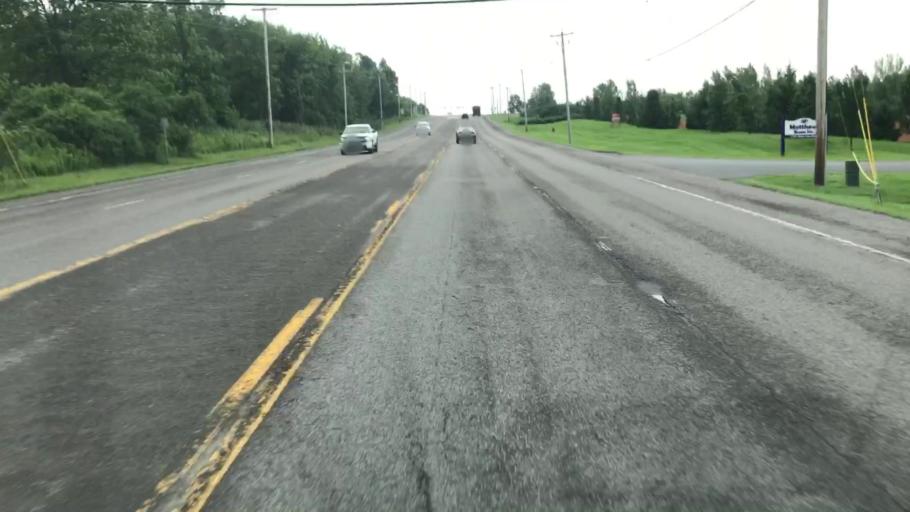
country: US
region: New York
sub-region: Onondaga County
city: Liverpool
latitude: 43.1463
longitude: -76.1880
